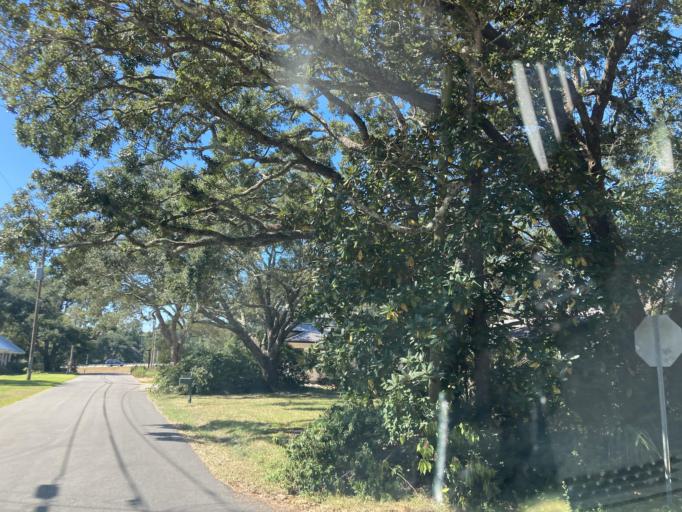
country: US
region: Mississippi
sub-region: Jackson County
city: Ocean Springs
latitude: 30.4118
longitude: -88.8375
